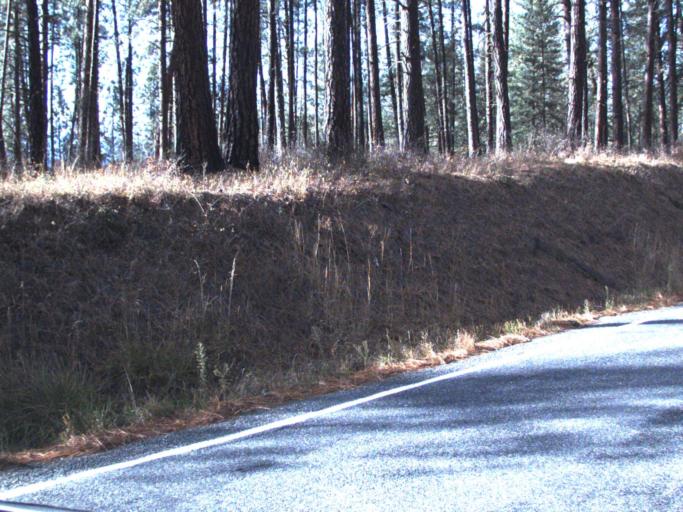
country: US
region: Washington
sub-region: Stevens County
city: Kettle Falls
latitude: 48.2963
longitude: -118.1447
